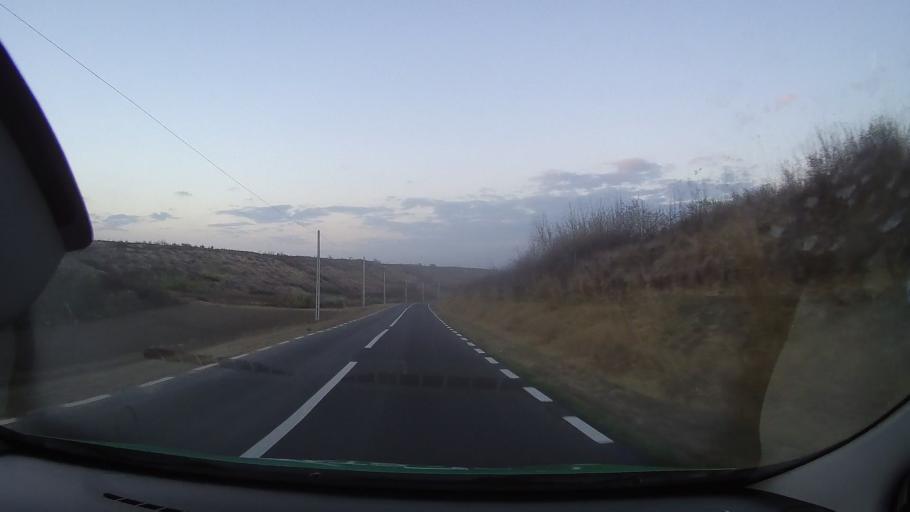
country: RO
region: Constanta
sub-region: Comuna Oltina
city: Oltina
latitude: 44.1367
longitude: 27.6662
